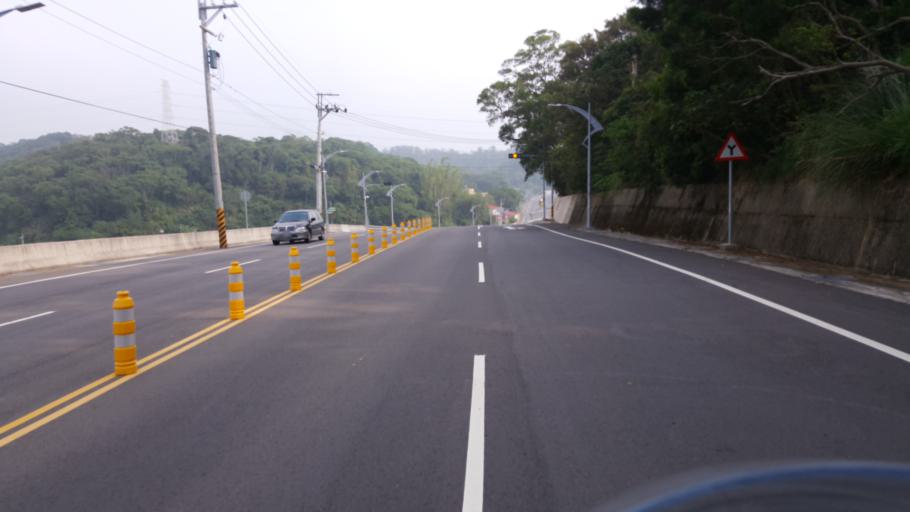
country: TW
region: Taiwan
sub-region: Hsinchu
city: Hsinchu
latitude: 24.7433
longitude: 120.9596
